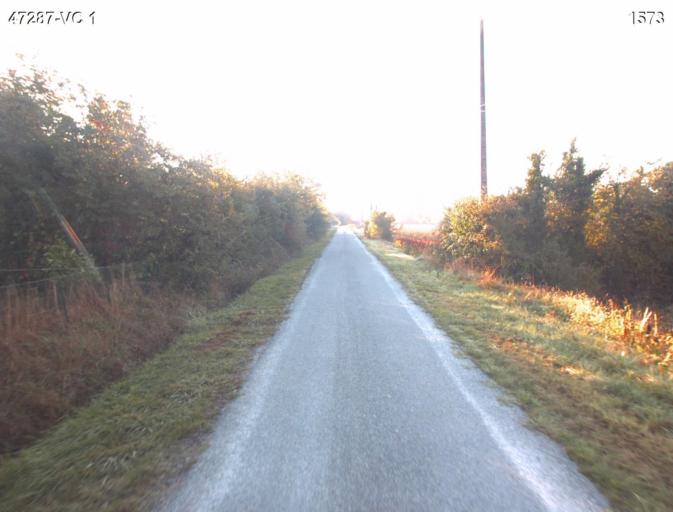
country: FR
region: Aquitaine
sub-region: Departement du Lot-et-Garonne
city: Sainte-Colombe-en-Bruilhois
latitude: 44.1351
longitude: 0.4480
